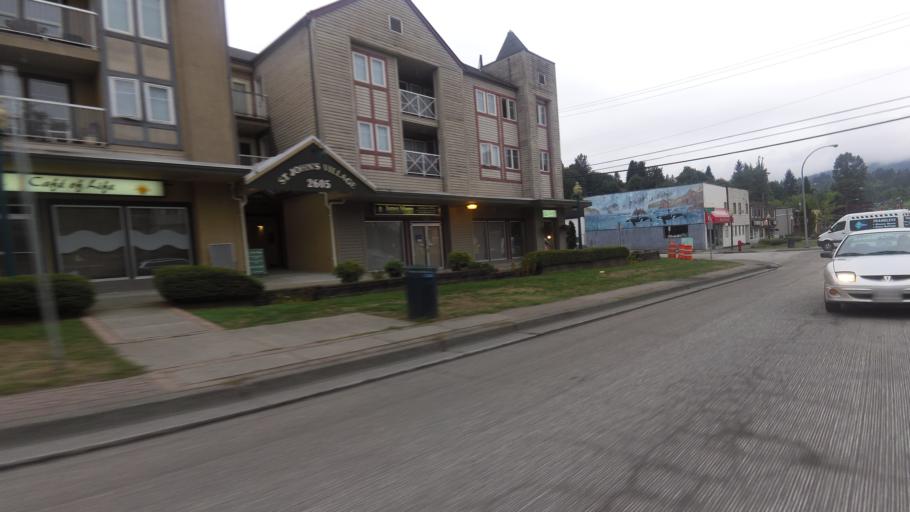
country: CA
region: British Columbia
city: Port Moody
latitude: 49.2767
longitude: -122.8542
